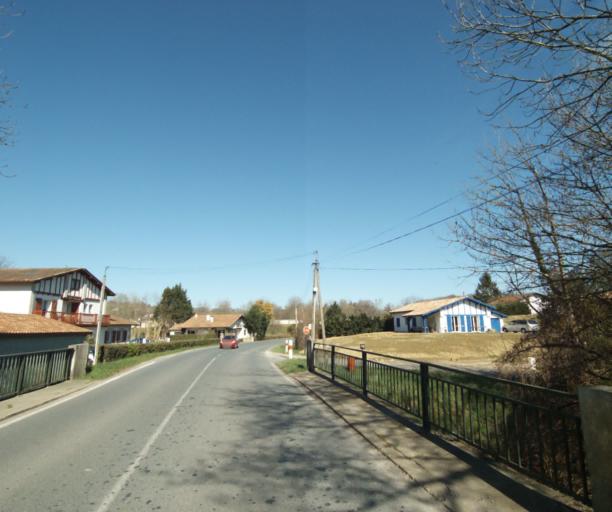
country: FR
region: Aquitaine
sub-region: Departement des Pyrenees-Atlantiques
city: Urrugne
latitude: 43.3602
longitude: -1.6923
